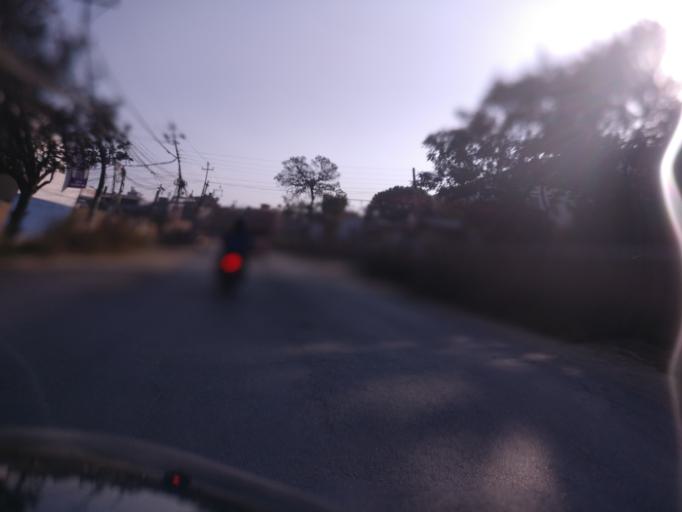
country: NP
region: Central Region
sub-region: Bagmati Zone
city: Patan
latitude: 27.6629
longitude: 85.3241
